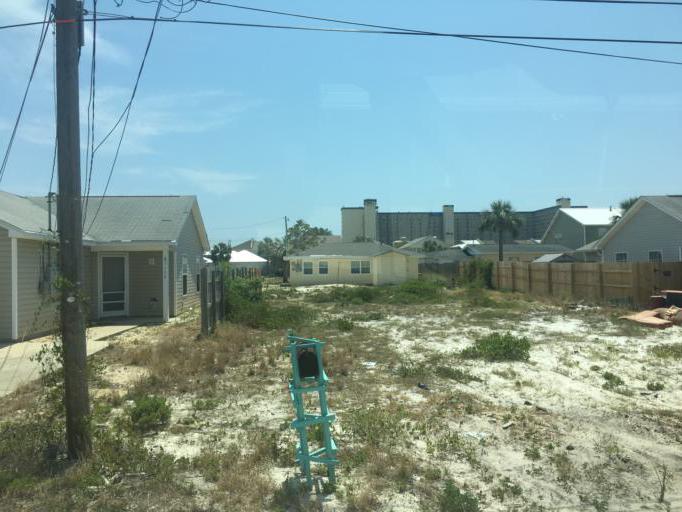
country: US
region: Florida
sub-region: Bay County
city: Lower Grand Lagoon
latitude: 30.1485
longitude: -85.7578
